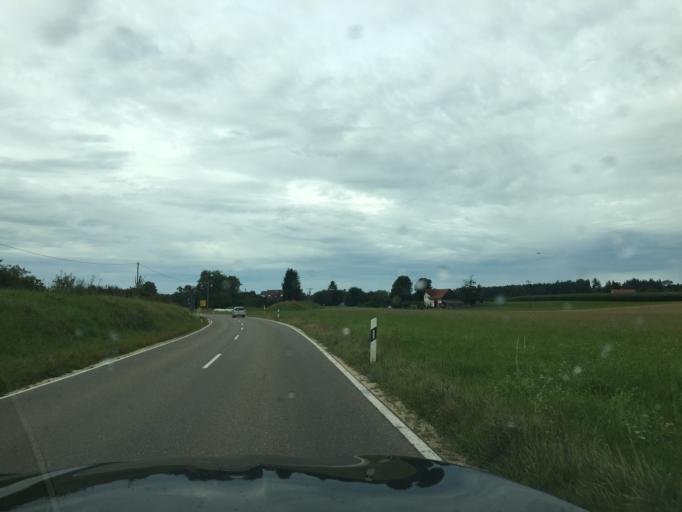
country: DE
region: Baden-Wuerttemberg
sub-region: Tuebingen Region
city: Wald
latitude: 47.9077
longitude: 9.1784
